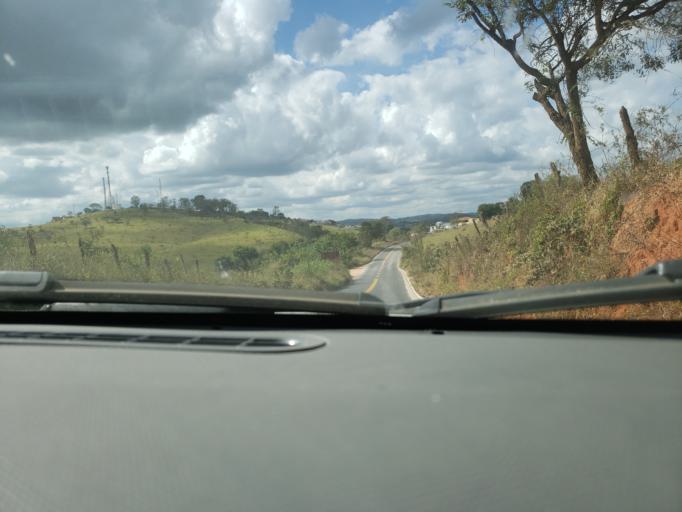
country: BR
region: Minas Gerais
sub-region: Campo Belo
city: Campo Belo
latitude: -20.9079
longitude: -45.2898
